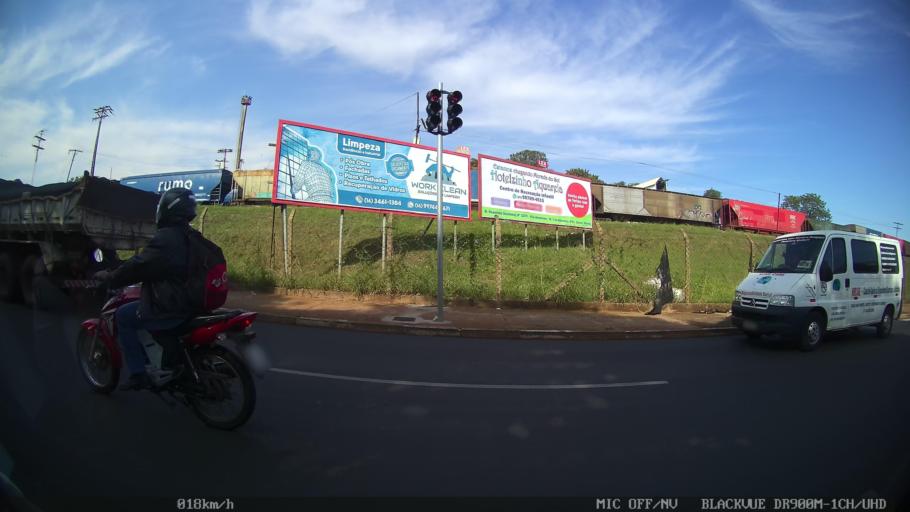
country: BR
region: Sao Paulo
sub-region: Araraquara
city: Araraquara
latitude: -21.7817
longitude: -48.1711
